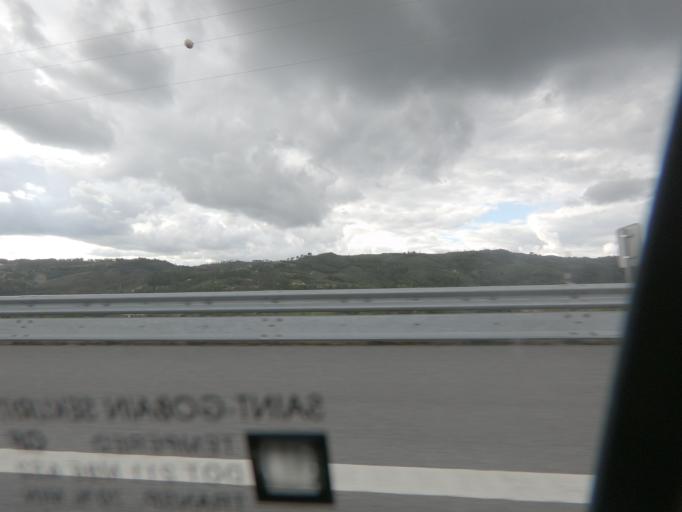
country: PT
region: Porto
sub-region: Amarante
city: Amarante
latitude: 41.2620
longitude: -8.0132
